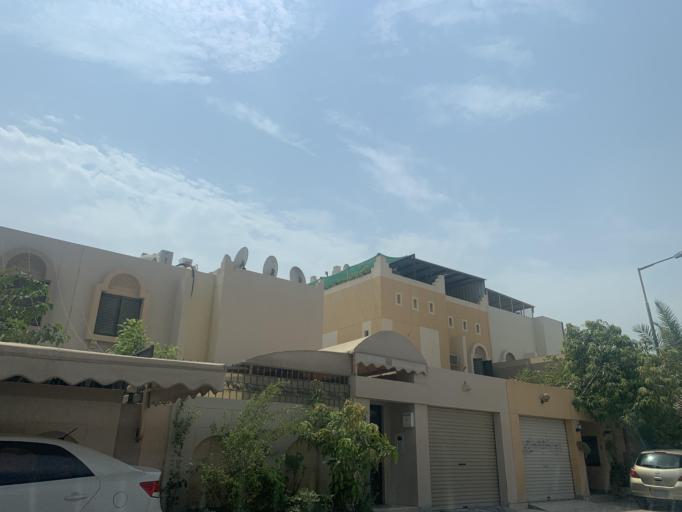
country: BH
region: Manama
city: Jidd Hafs
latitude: 26.2081
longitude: 50.5084
